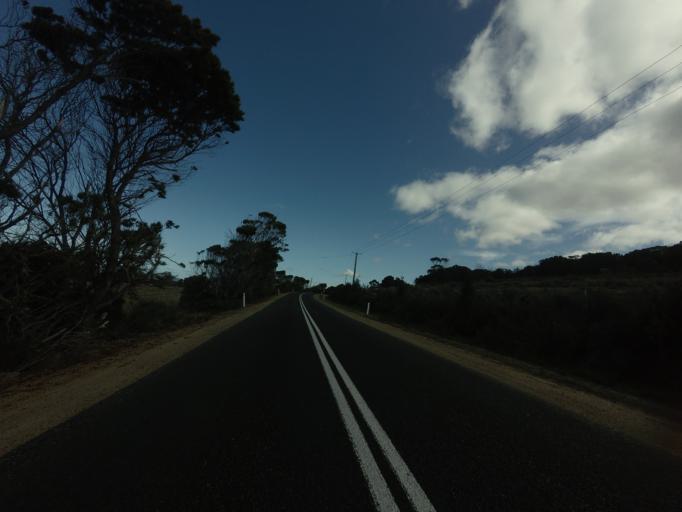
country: AU
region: Tasmania
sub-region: Break O'Day
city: St Helens
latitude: -41.7946
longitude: 148.2624
